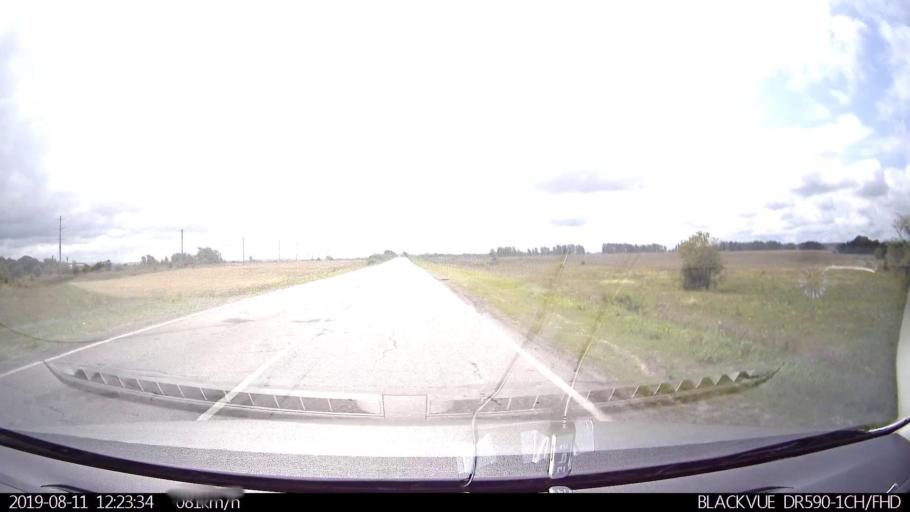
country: RU
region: Ulyanovsk
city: Ignatovka
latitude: 53.8938
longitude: 47.9503
